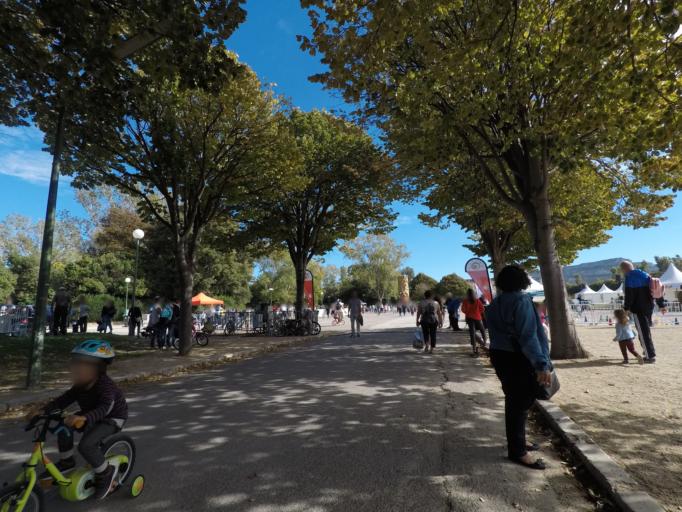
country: FR
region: Provence-Alpes-Cote d'Azur
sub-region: Departement des Bouches-du-Rhone
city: Marseille 08
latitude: 43.2603
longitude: 5.3806
